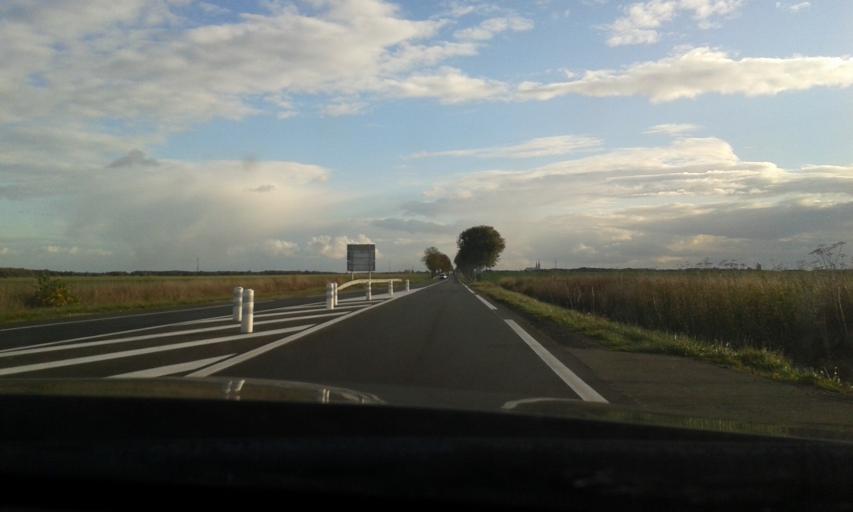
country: FR
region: Centre
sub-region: Departement d'Eure-et-Loir
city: Leves
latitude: 48.4999
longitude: 1.4672
